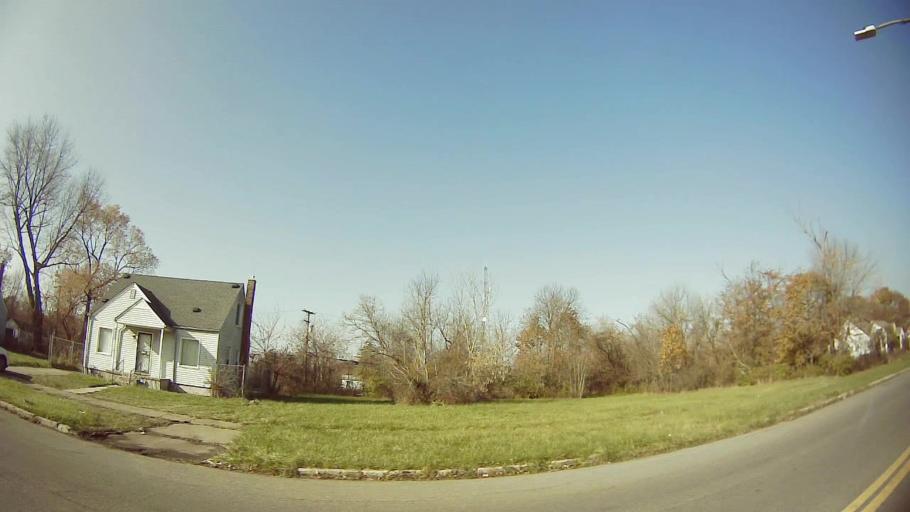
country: US
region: Michigan
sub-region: Wayne County
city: Dearborn
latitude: 42.3694
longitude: -83.1680
